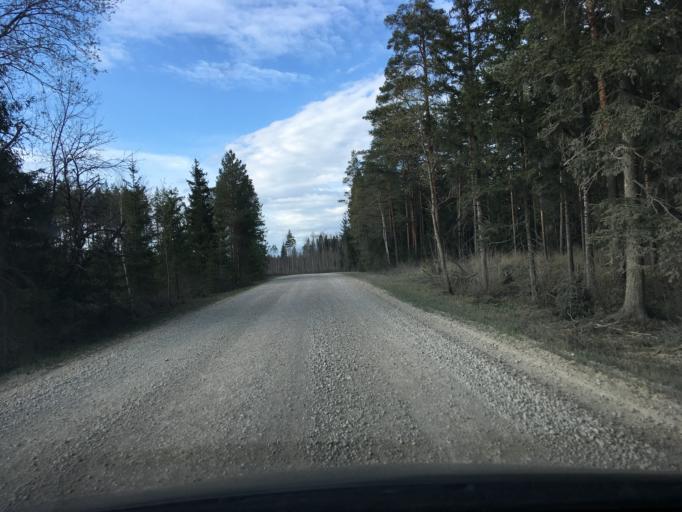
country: EE
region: Raplamaa
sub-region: Maerjamaa vald
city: Marjamaa
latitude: 58.9564
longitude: 24.3258
